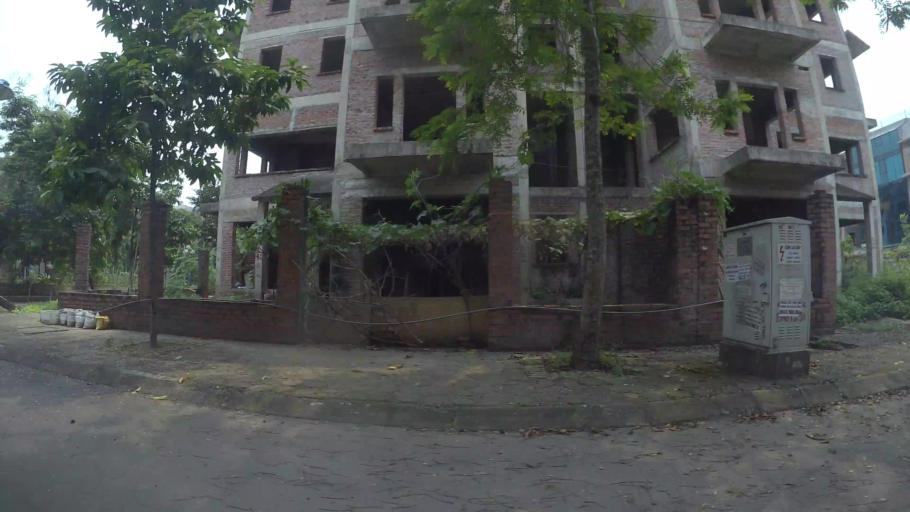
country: VN
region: Ha Noi
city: Cau Dien
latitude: 21.0251
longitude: 105.7451
